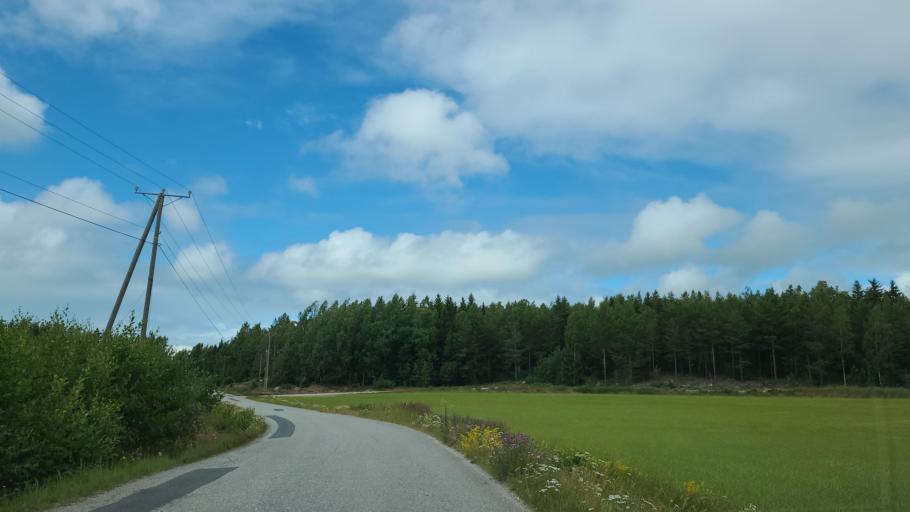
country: FI
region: Varsinais-Suomi
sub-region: Aboland-Turunmaa
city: Nagu
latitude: 60.1736
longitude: 21.9793
